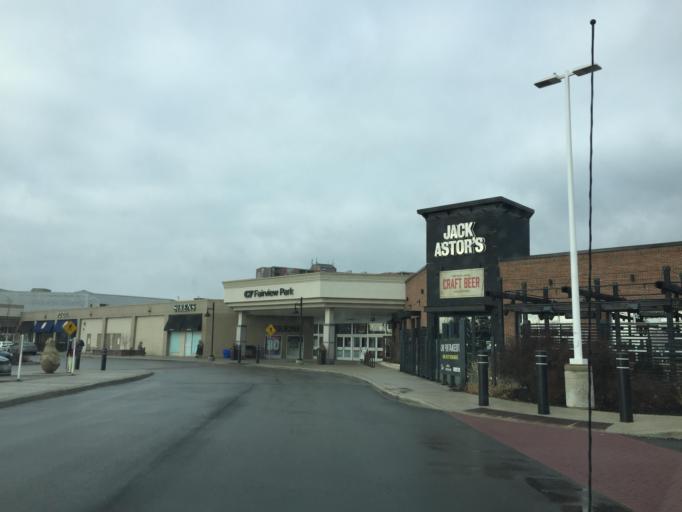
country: CA
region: Ontario
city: Kitchener
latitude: 43.4233
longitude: -80.4388
